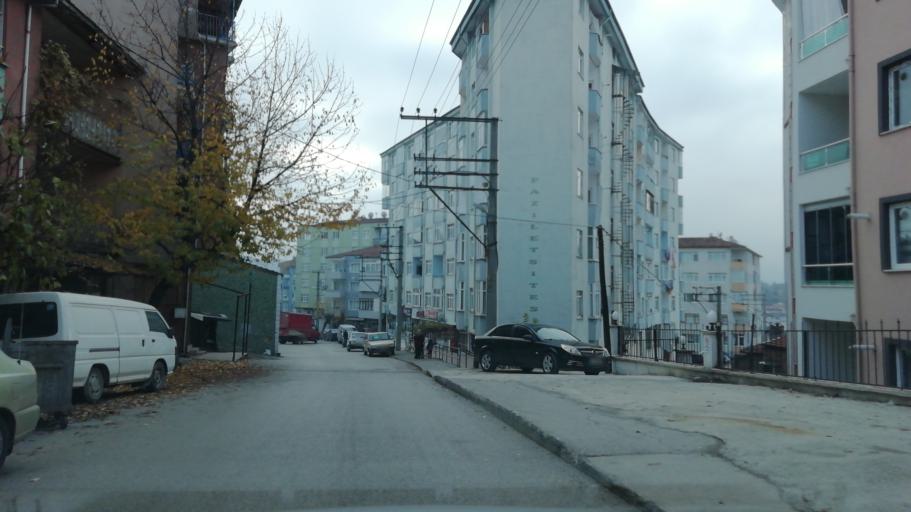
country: TR
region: Karabuk
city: Karabuk
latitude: 41.2079
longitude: 32.6267
